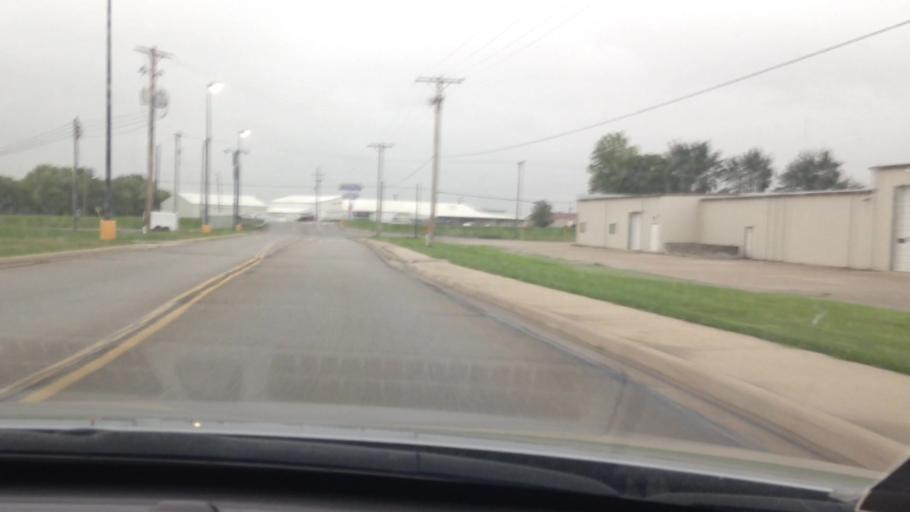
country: US
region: Kansas
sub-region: Brown County
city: Hiawatha
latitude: 39.8476
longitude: -95.5616
